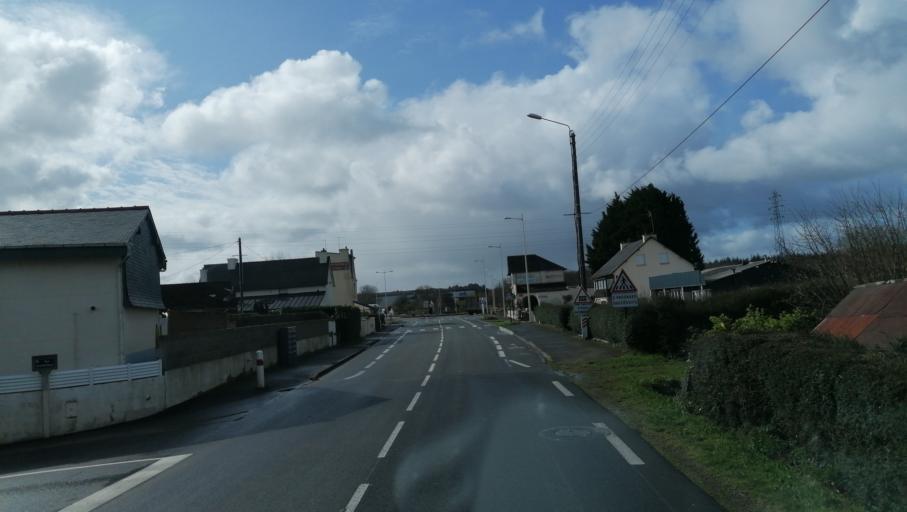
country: FR
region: Brittany
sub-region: Departement des Cotes-d'Armor
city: Ploufragan
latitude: 48.4730
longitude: -2.8011
